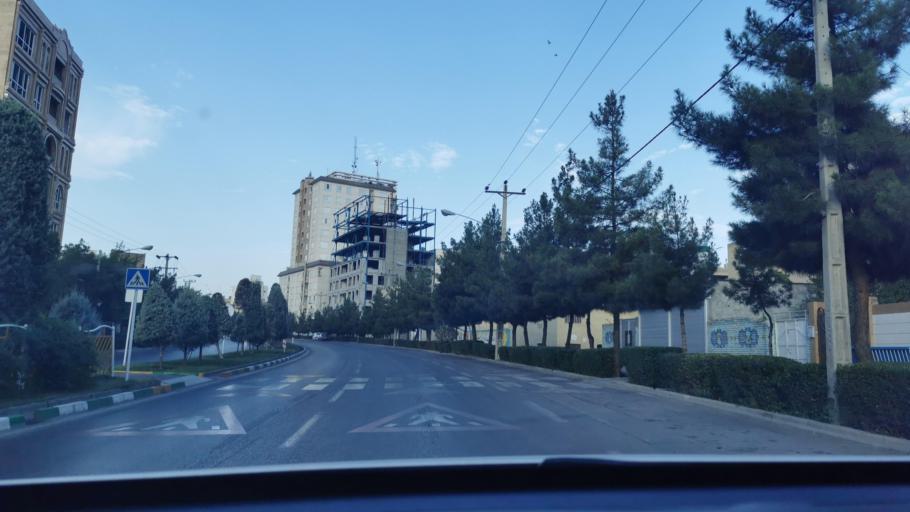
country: IR
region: Razavi Khorasan
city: Mashhad
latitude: 36.3587
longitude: 59.5041
